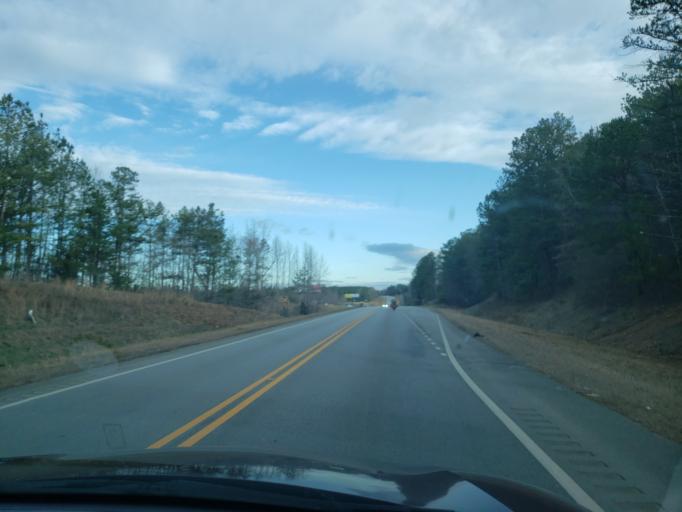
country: US
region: Alabama
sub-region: Randolph County
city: Wedowee
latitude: 33.3370
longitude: -85.4895
